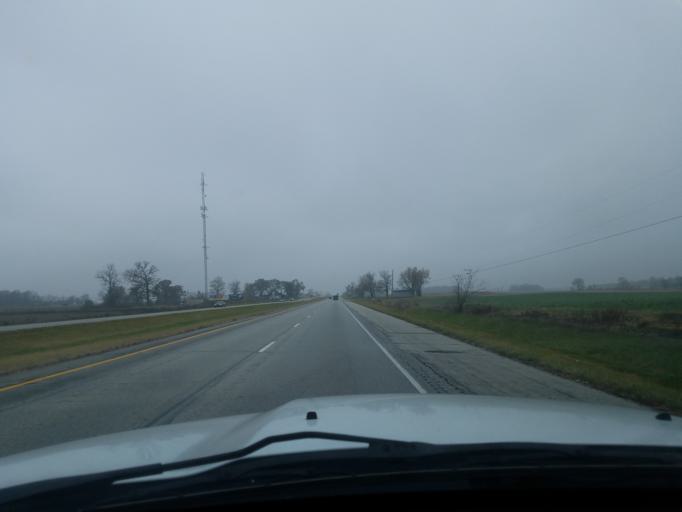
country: US
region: Indiana
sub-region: Hamilton County
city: Arcadia
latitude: 40.1952
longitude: -86.1281
